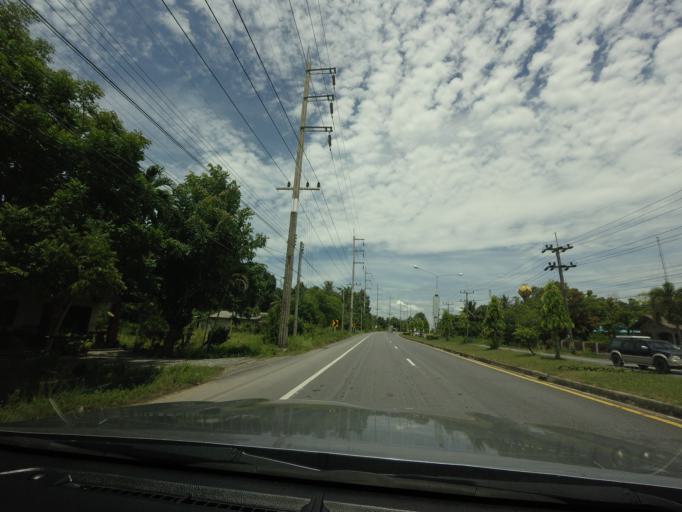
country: TH
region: Songkhla
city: Sathing Phra
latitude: 7.5606
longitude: 100.4132
